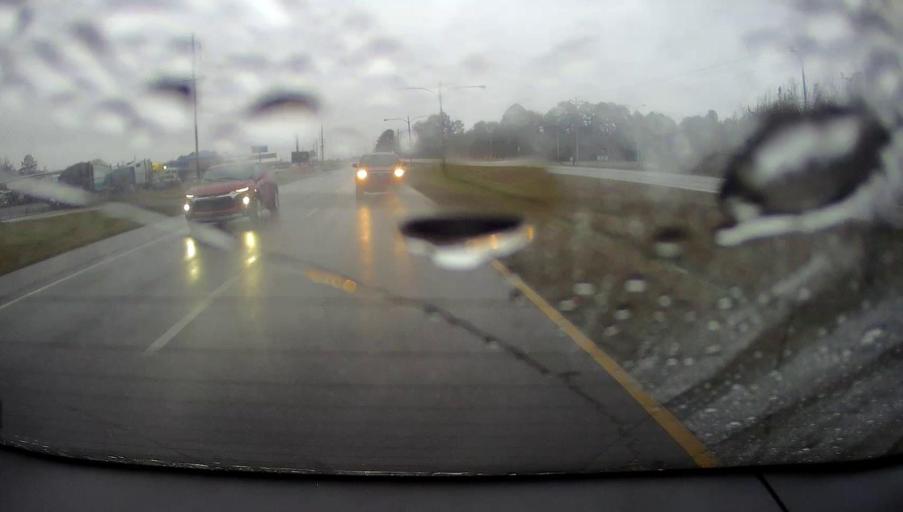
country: US
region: Alabama
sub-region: Morgan County
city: Hartselle
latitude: 34.4190
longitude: -86.9245
